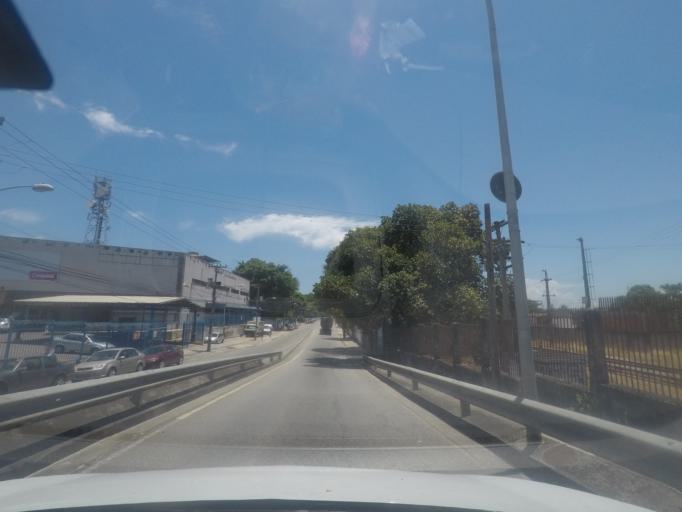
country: BR
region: Rio de Janeiro
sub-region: Itaguai
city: Itaguai
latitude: -22.9169
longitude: -43.6860
